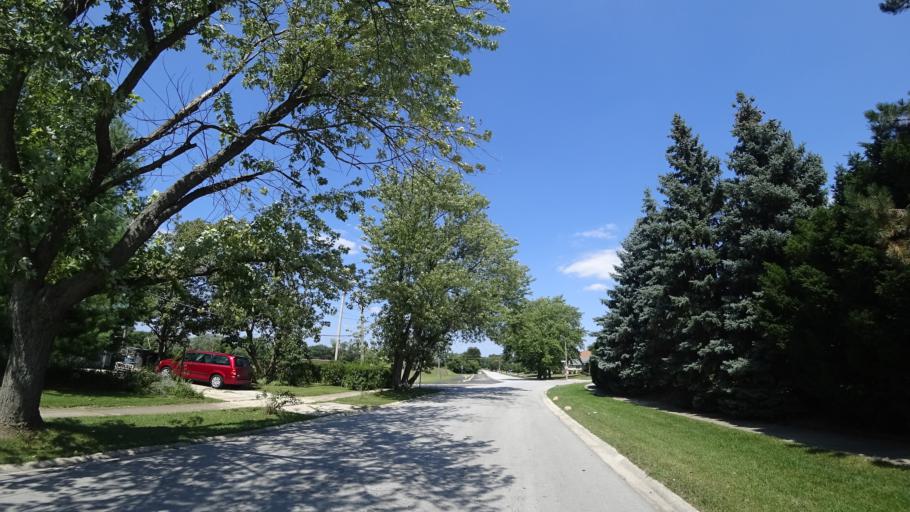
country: US
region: Illinois
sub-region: Cook County
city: Orland Park
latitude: 41.6255
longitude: -87.8341
